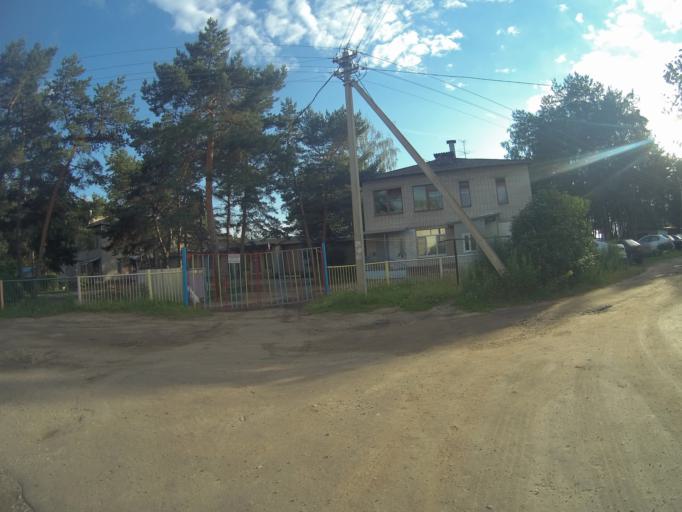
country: RU
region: Vladimir
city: Kommunar
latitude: 56.1226
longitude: 40.4626
